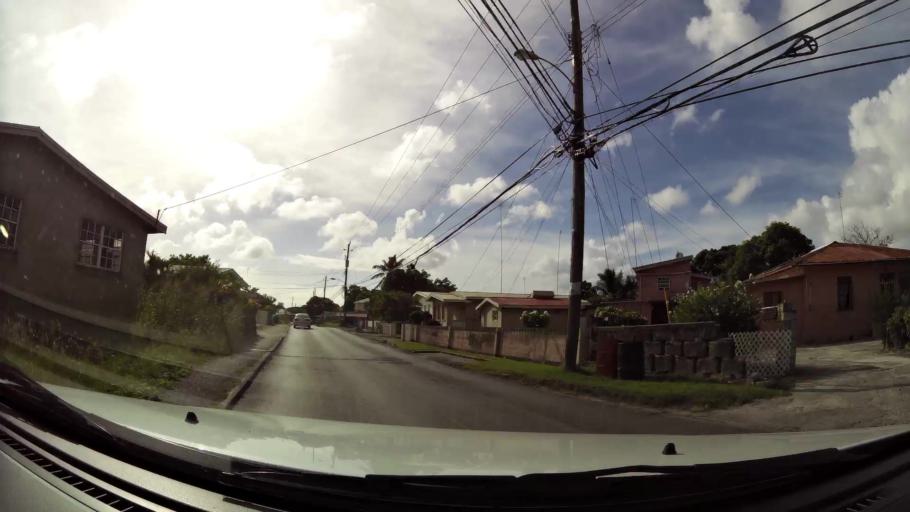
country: BB
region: Saint Michael
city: Bridgetown
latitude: 13.0850
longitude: -59.5907
